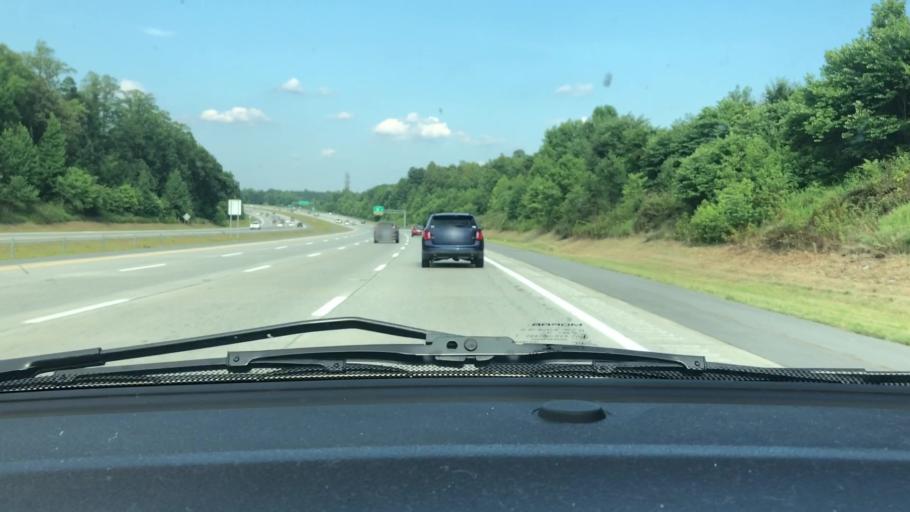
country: US
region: North Carolina
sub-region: Guilford County
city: Pleasant Garden
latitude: 35.9969
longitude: -79.7669
